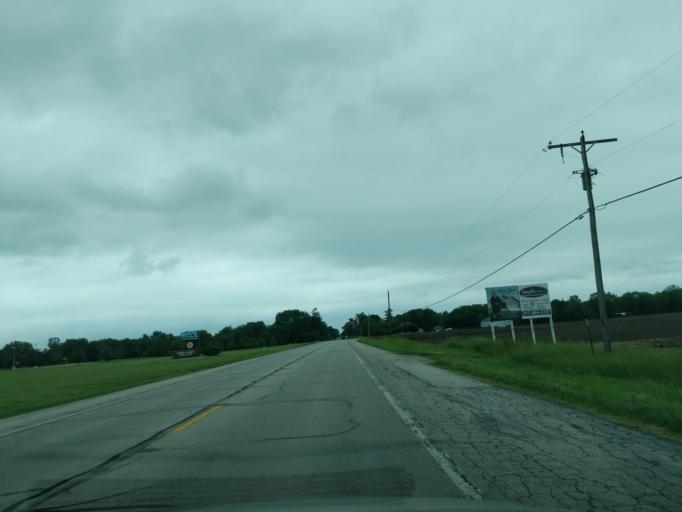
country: US
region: Indiana
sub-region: Hamilton County
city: Arcadia
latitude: 40.1645
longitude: -86.0132
